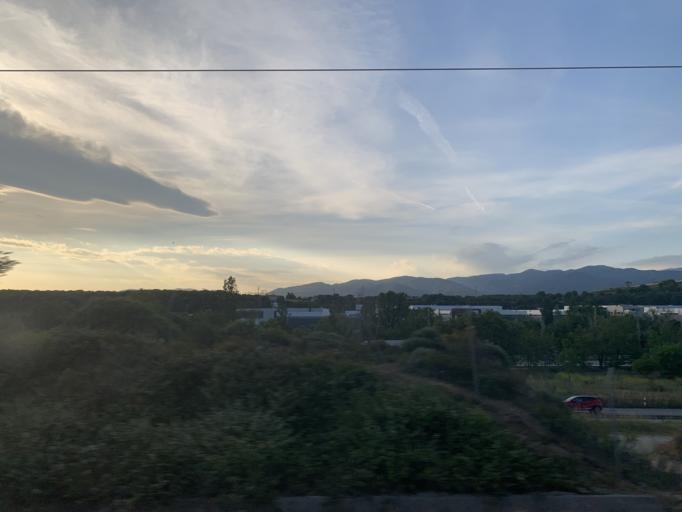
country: ES
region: Catalonia
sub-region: Provincia de Barcelona
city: Llinars del Valles
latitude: 41.6251
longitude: 2.3774
